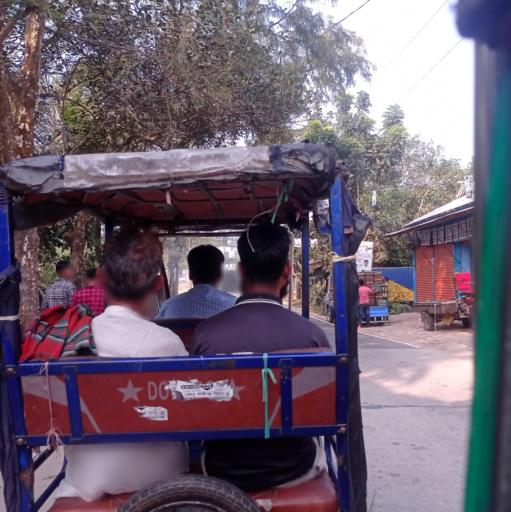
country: BD
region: Dhaka
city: Bhairab Bazar
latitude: 24.0368
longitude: 90.8322
